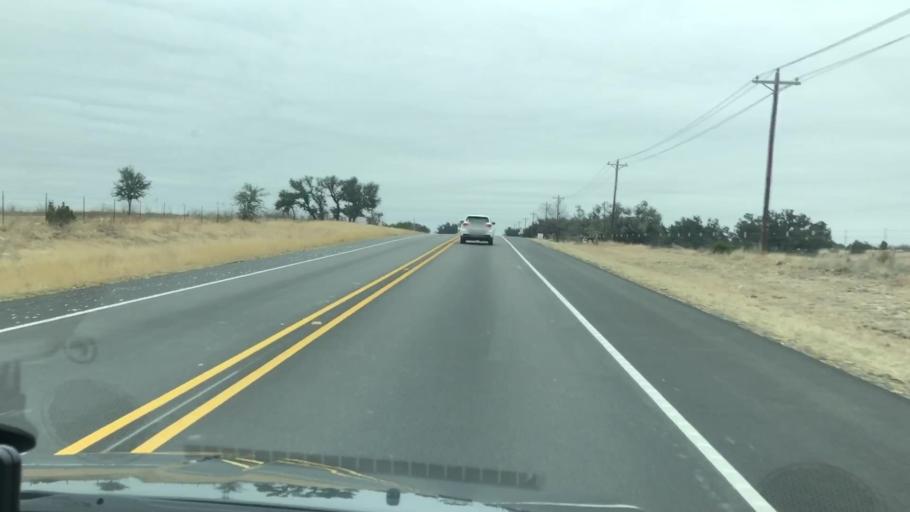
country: US
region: Texas
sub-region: Erath County
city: Stephenville
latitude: 32.3172
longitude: -98.1826
